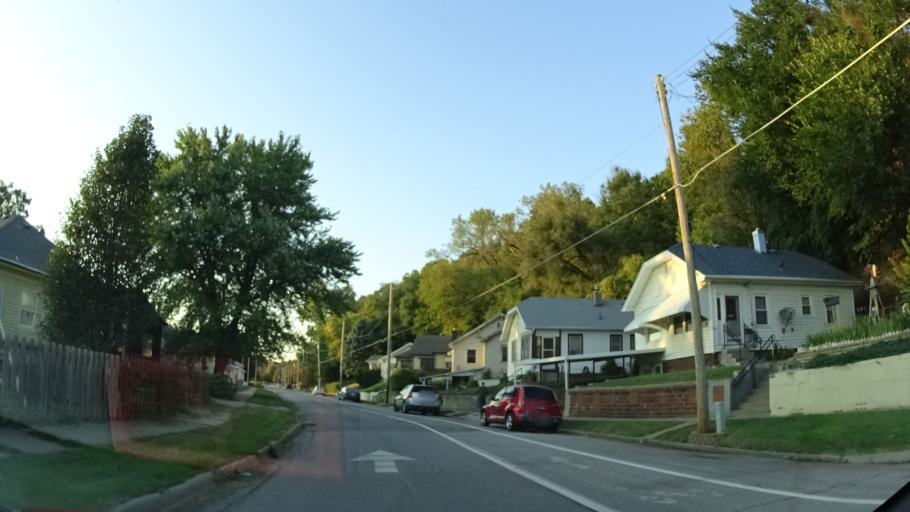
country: US
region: Iowa
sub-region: Pottawattamie County
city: Council Bluffs
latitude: 41.2652
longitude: -95.8516
